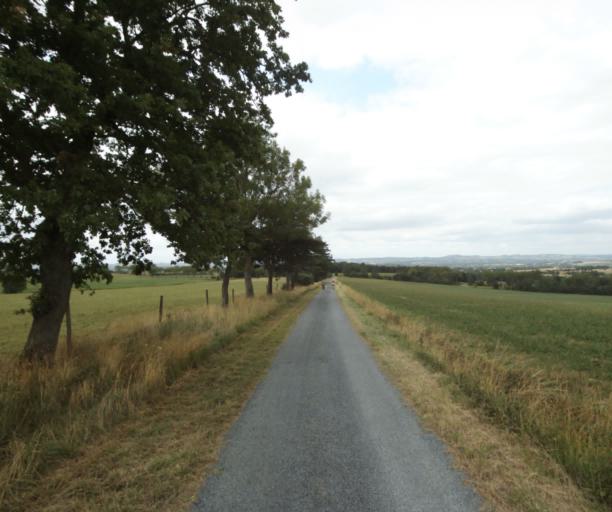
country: FR
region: Midi-Pyrenees
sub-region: Departement du Tarn
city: Soreze
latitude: 43.4610
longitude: 2.0888
